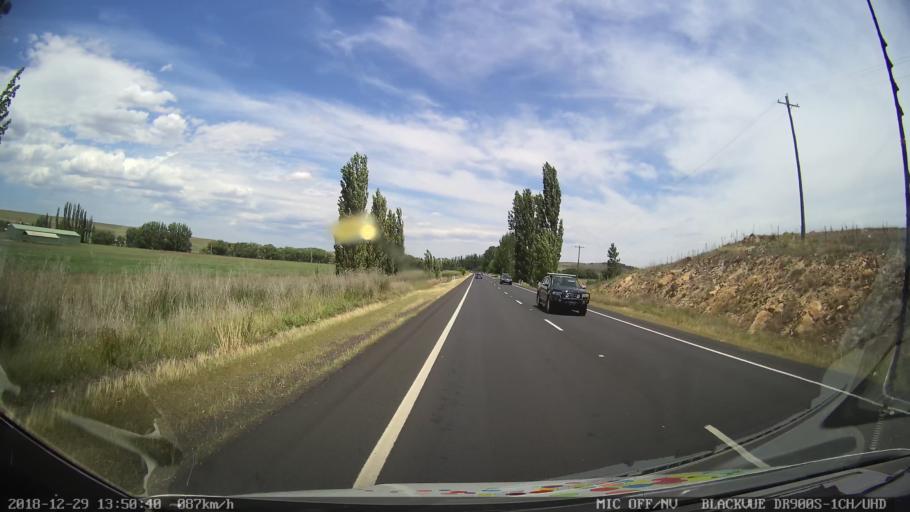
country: AU
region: New South Wales
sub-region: Cooma-Monaro
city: Cooma
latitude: -36.1709
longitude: 149.1539
